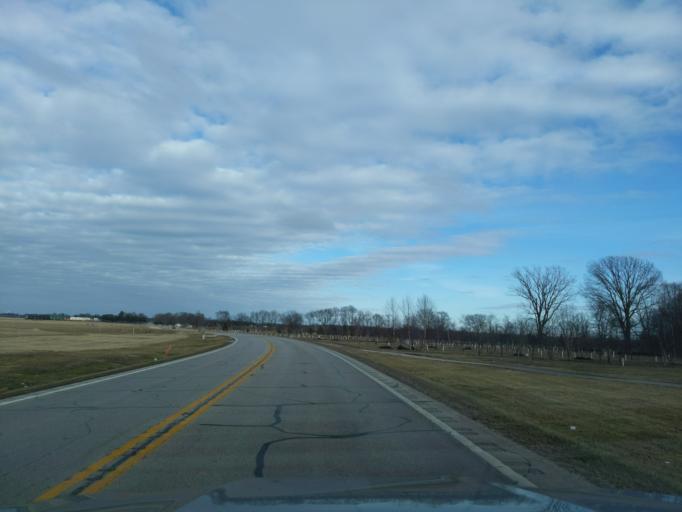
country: US
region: Indiana
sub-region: Tippecanoe County
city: Shadeland
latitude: 40.3598
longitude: -86.9707
